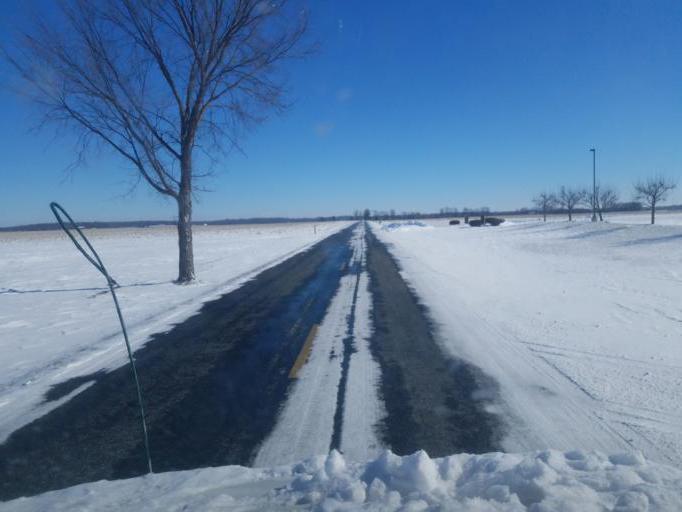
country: US
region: Ohio
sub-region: Delaware County
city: Delaware
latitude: 40.2878
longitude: -83.0086
